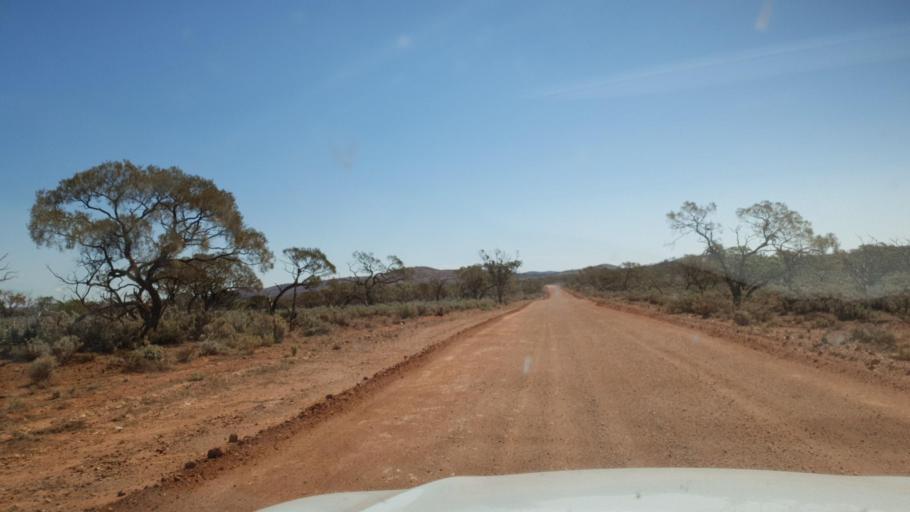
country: AU
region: South Australia
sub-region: Whyalla
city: Whyalla
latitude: -32.6168
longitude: 136.7642
